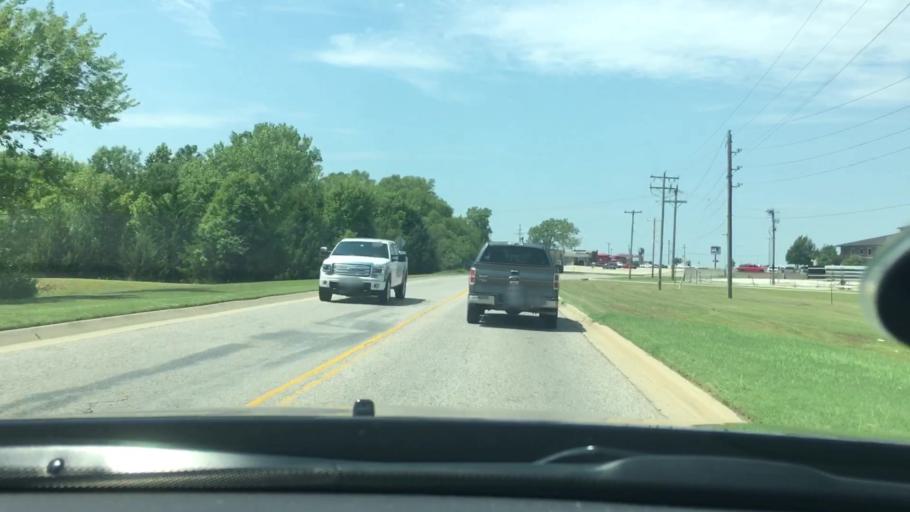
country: US
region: Oklahoma
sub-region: Pontotoc County
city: Ada
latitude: 34.7909
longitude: -96.6484
